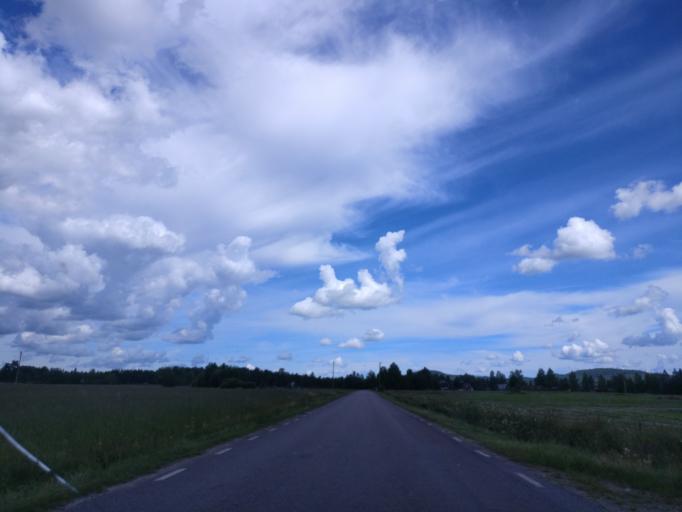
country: SE
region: Vaermland
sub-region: Hagfors Kommun
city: Ekshaerad
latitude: 60.1253
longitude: 13.4553
